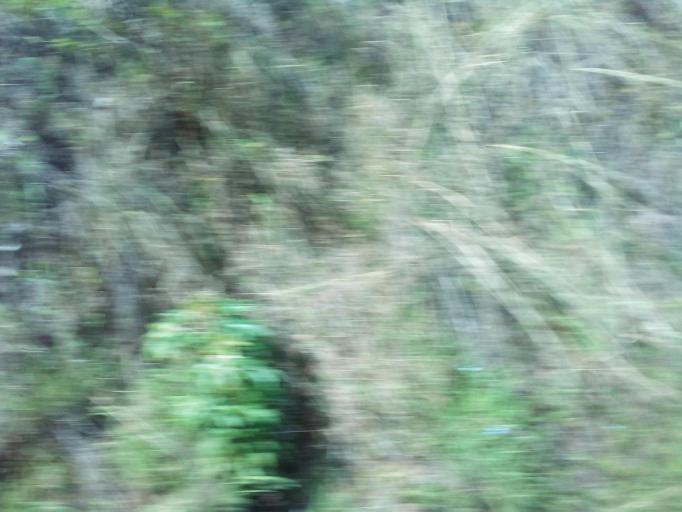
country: BR
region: Minas Gerais
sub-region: Caete
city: Caete
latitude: -19.8875
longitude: -43.7596
